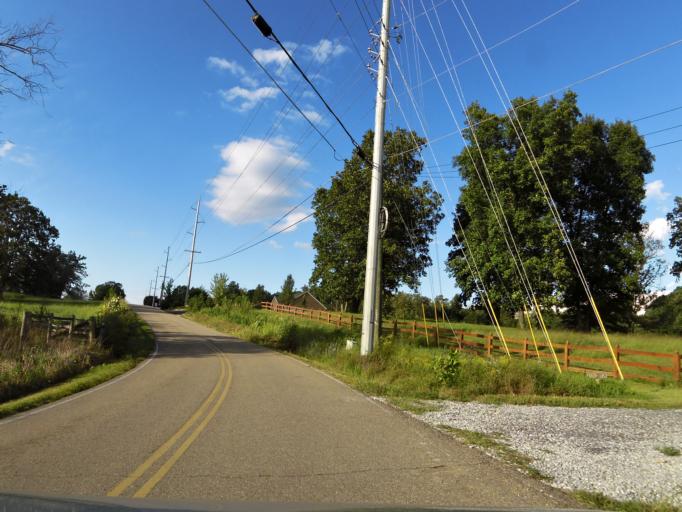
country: US
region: Tennessee
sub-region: Grainger County
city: Blaine
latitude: 36.1482
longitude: -83.7399
